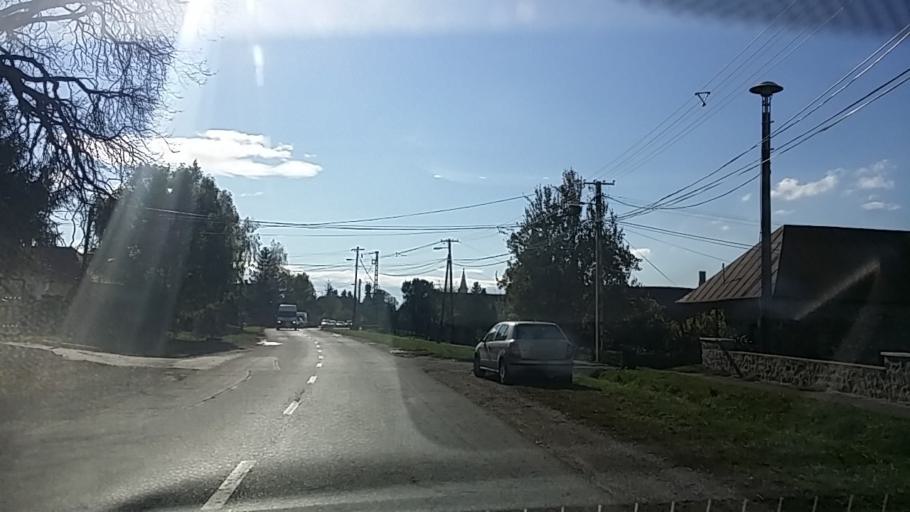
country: HU
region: Borsod-Abauj-Zemplen
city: Gonc
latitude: 48.4204
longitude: 21.2335
